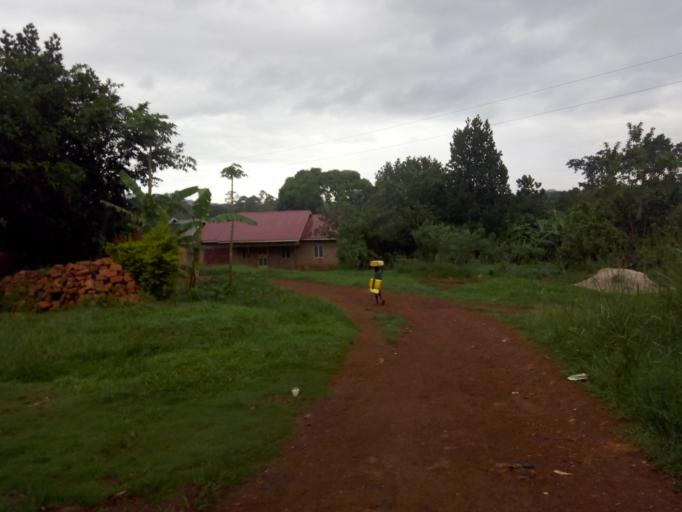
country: UG
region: Western Region
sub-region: Masindi District
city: Masindi
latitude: 1.6814
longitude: 31.7141
